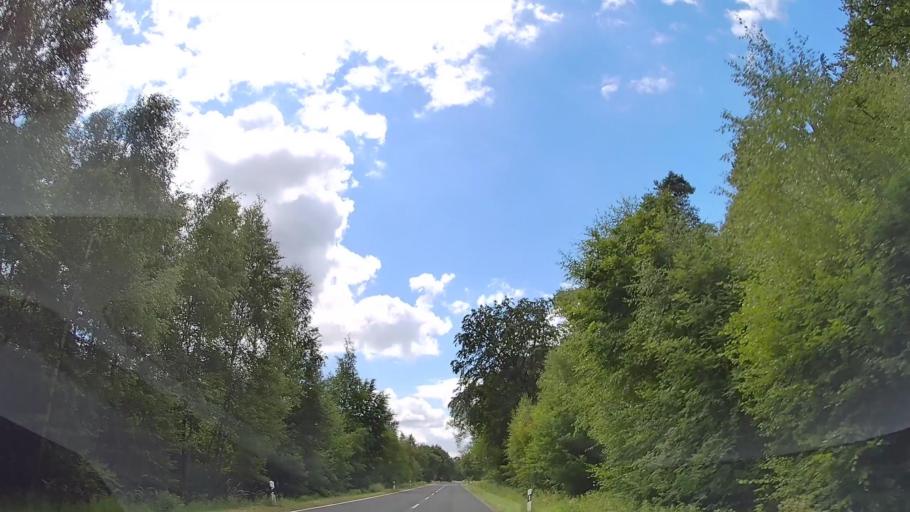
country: DE
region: North Rhine-Westphalia
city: Rahden
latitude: 52.4145
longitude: 8.5209
